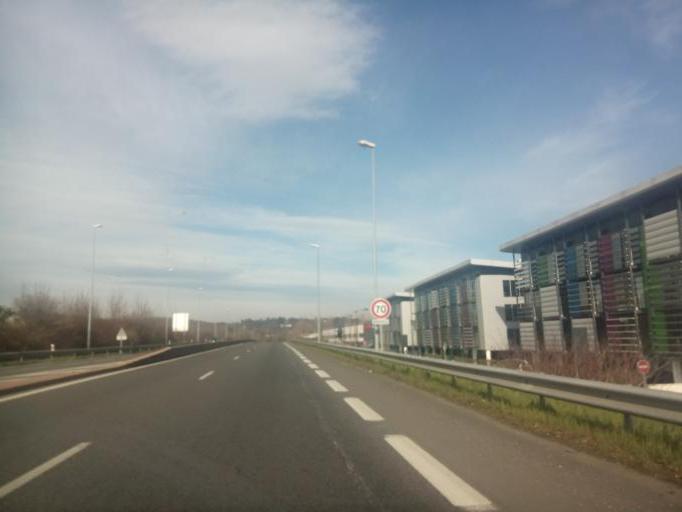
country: FR
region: Rhone-Alpes
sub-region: Departement du Rhone
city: Brignais
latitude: 45.6847
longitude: 4.7668
